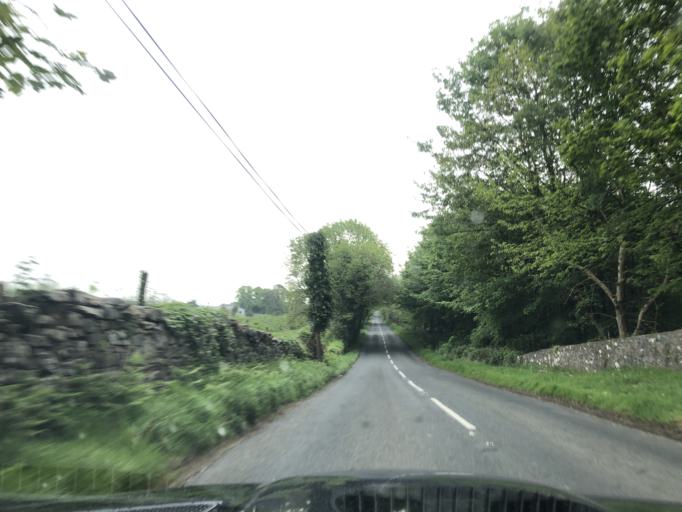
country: GB
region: Northern Ireland
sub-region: Down District
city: Castlewellan
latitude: 54.2236
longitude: -5.9630
